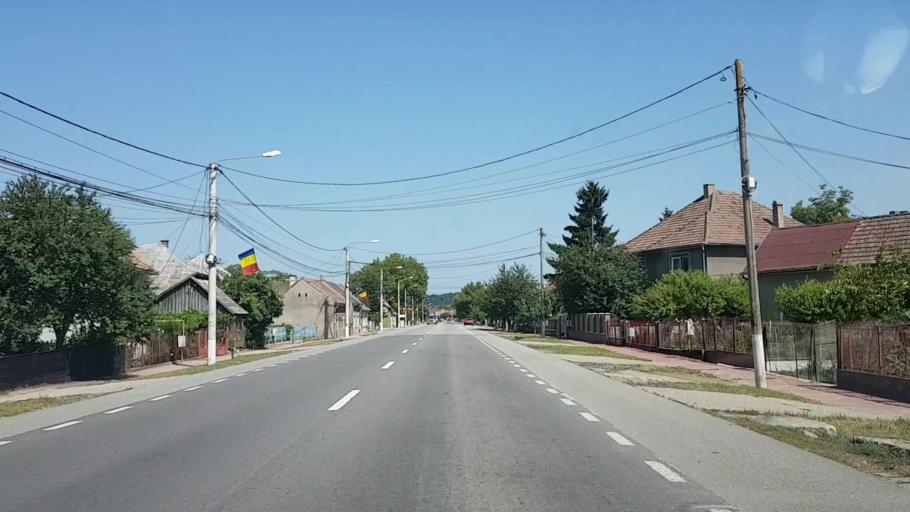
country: RO
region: Bistrita-Nasaud
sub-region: Comuna Beclean
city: Beclean
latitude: 47.1750
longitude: 24.1611
